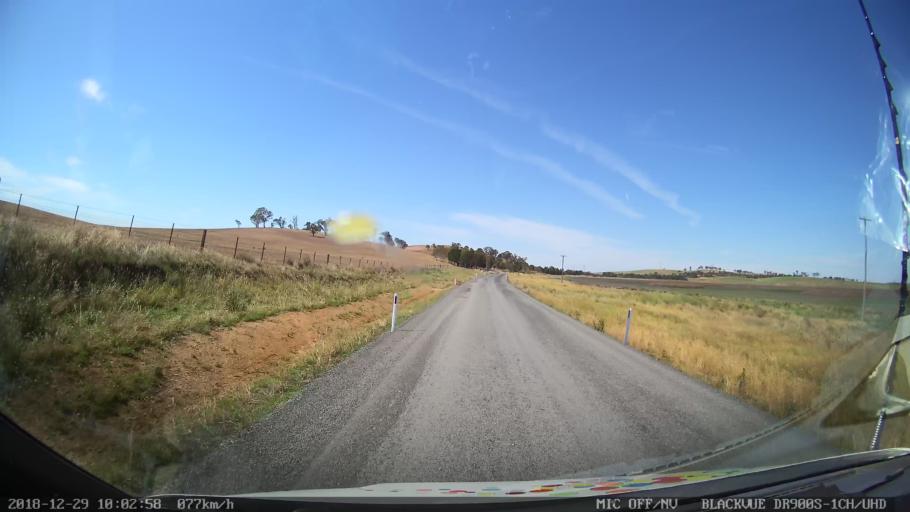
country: AU
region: New South Wales
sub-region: Goulburn Mulwaree
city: Goulburn
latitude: -34.8058
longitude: 149.4613
